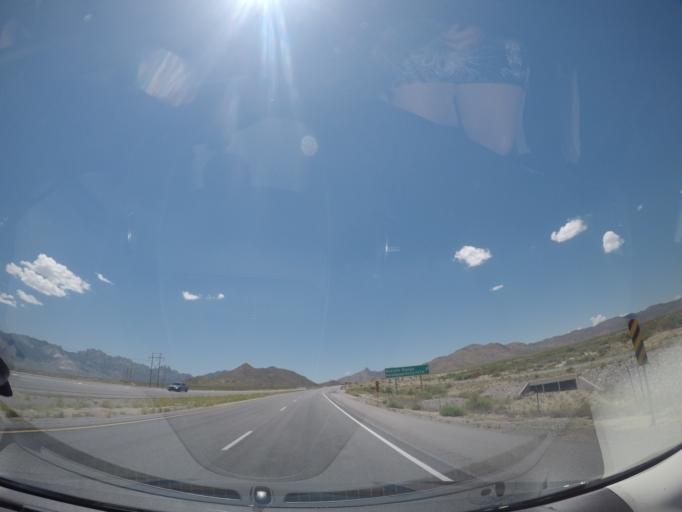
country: US
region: New Mexico
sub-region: Dona Ana County
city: White Sands
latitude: 32.4387
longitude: -106.4683
